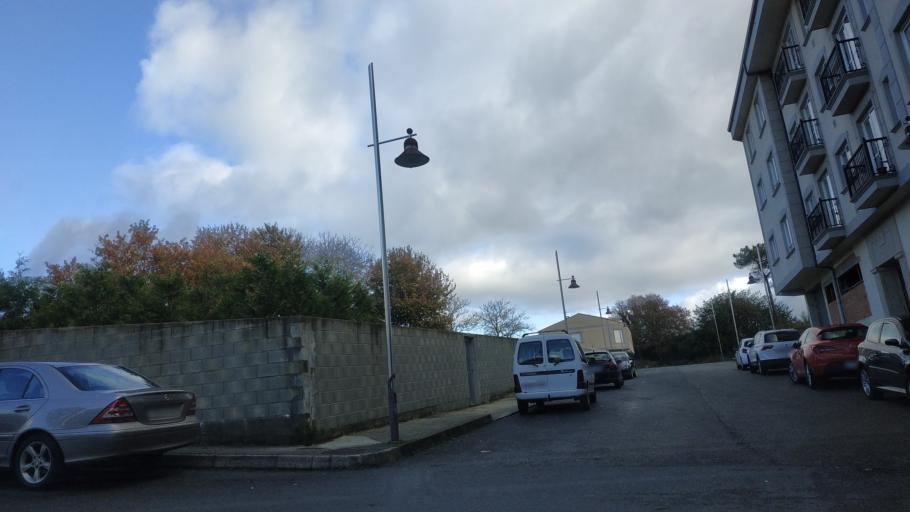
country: ES
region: Galicia
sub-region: Provincia de Pontevedra
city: Silleda
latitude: 42.7922
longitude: -8.1699
